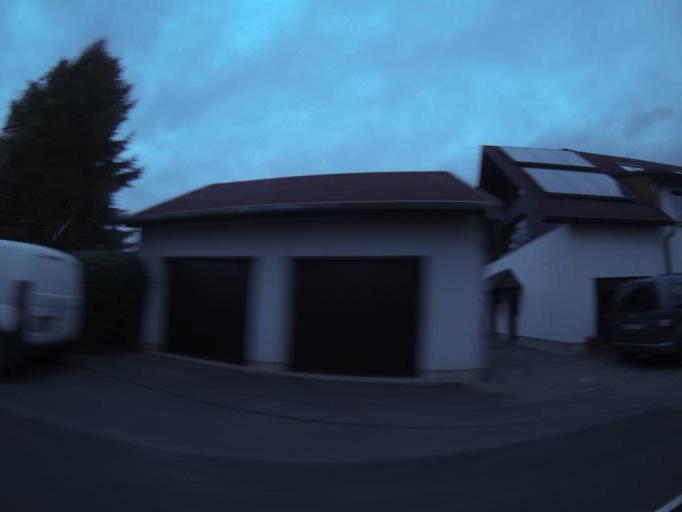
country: DE
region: Thuringia
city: Saara
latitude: 50.9301
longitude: 12.4216
